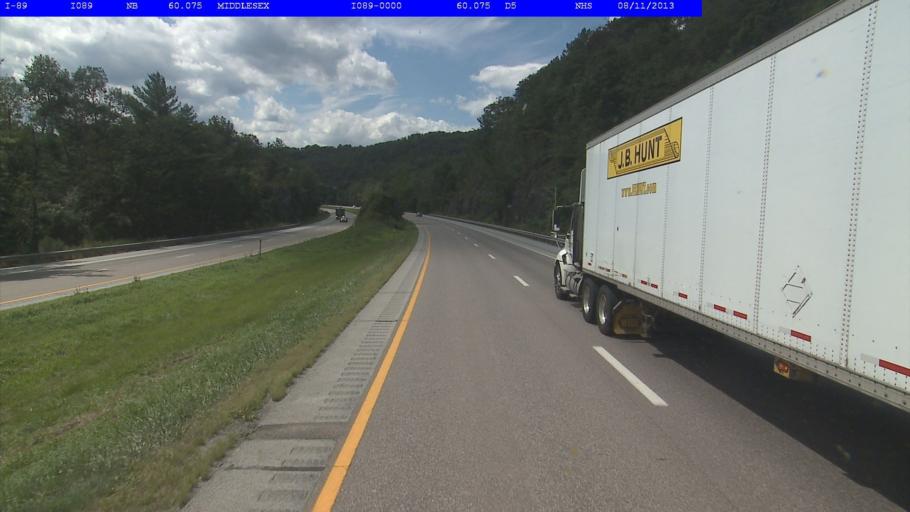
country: US
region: Vermont
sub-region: Washington County
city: Waterbury
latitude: 44.3145
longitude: -72.6994
